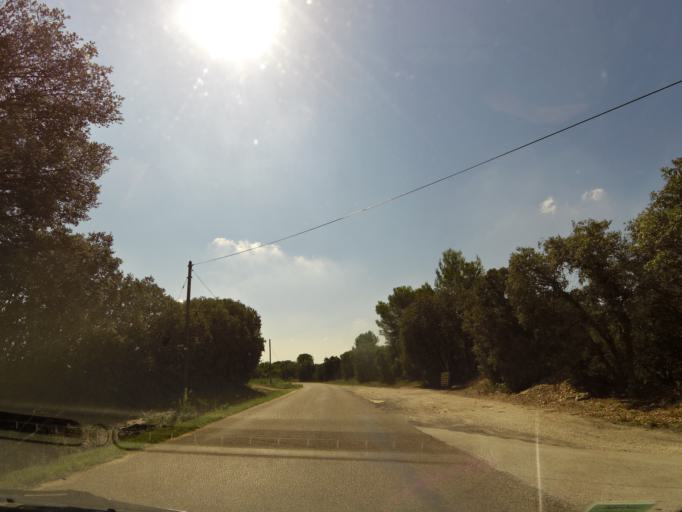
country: FR
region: Languedoc-Roussillon
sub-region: Departement du Gard
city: Villevieille
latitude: 43.7956
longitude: 4.1186
